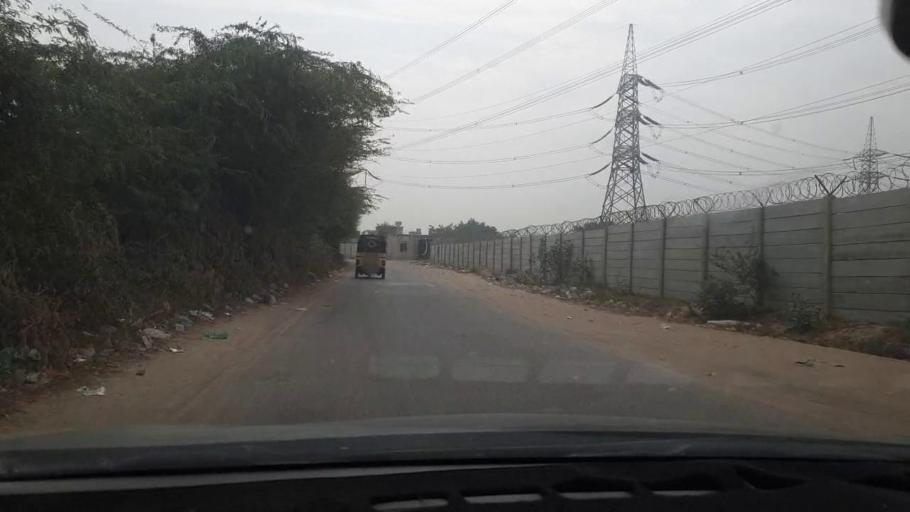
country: PK
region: Sindh
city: Malir Cantonment
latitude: 24.9095
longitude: 67.2855
